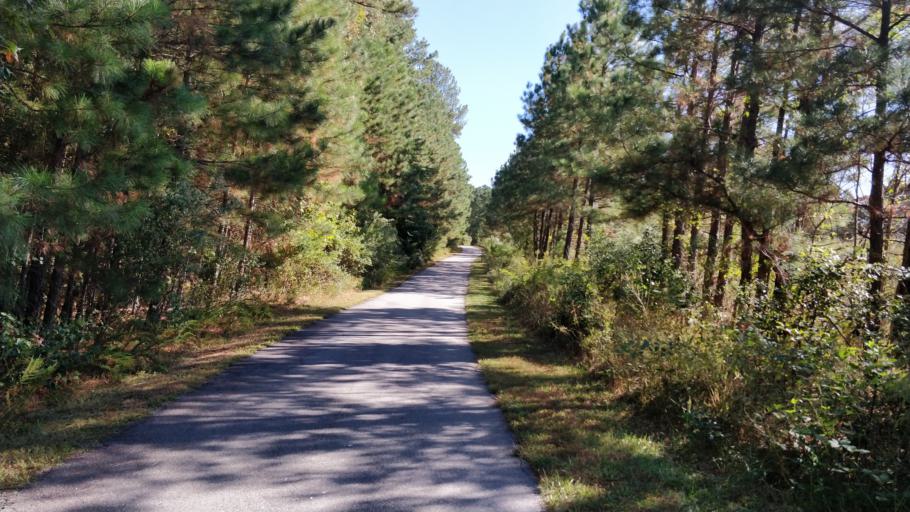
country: US
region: North Carolina
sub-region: Wake County
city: Morrisville
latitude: 35.8353
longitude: -78.8431
